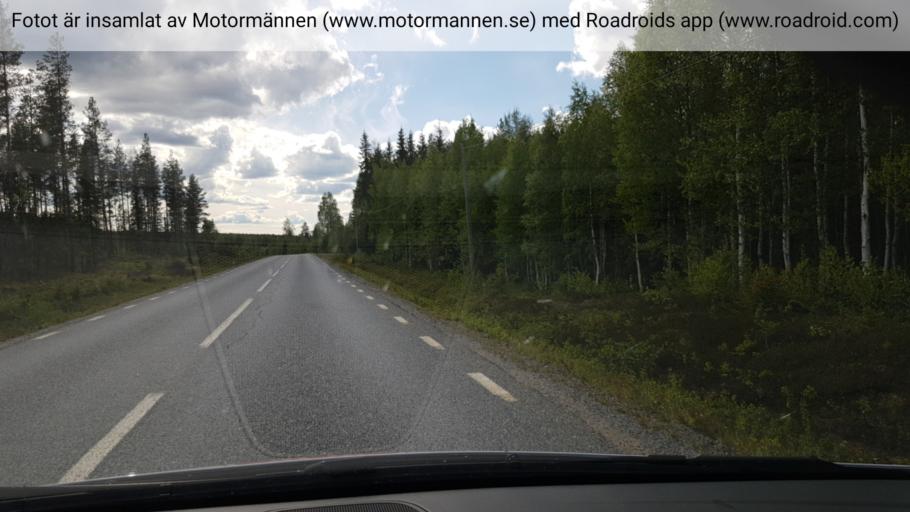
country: SE
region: Vaesterbotten
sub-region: Skelleftea Kommun
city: Burtraesk
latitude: 64.3861
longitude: 20.2791
